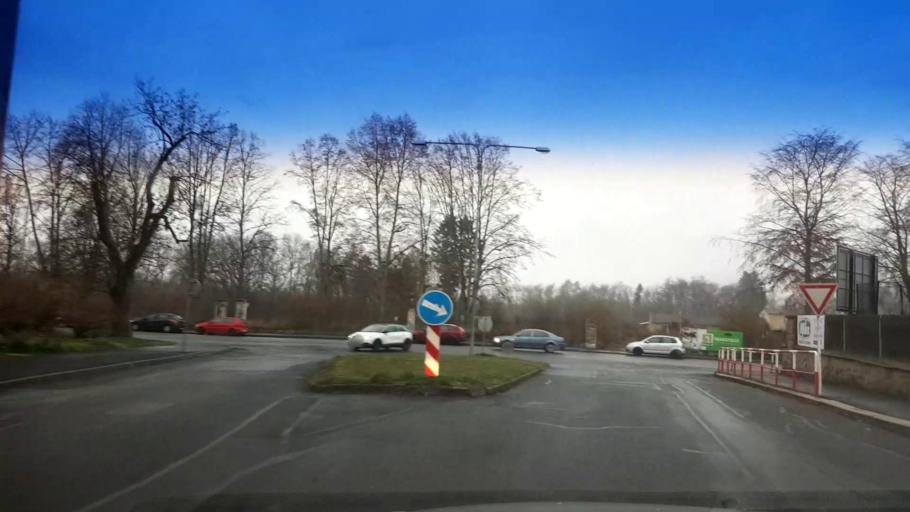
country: CZ
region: Karlovarsky
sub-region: Okres Cheb
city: Cheb
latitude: 50.0686
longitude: 12.3634
